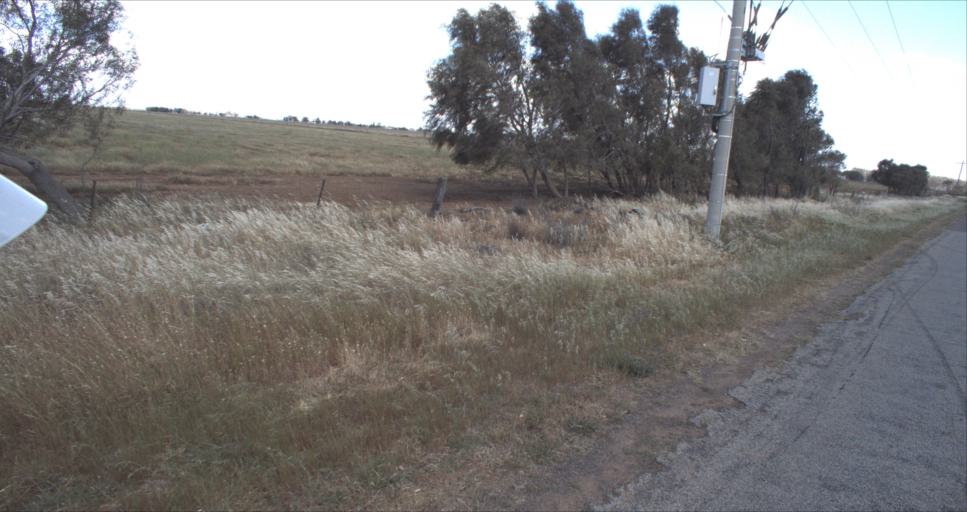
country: AU
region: New South Wales
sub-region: Leeton
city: Leeton
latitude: -34.5263
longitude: 146.2209
